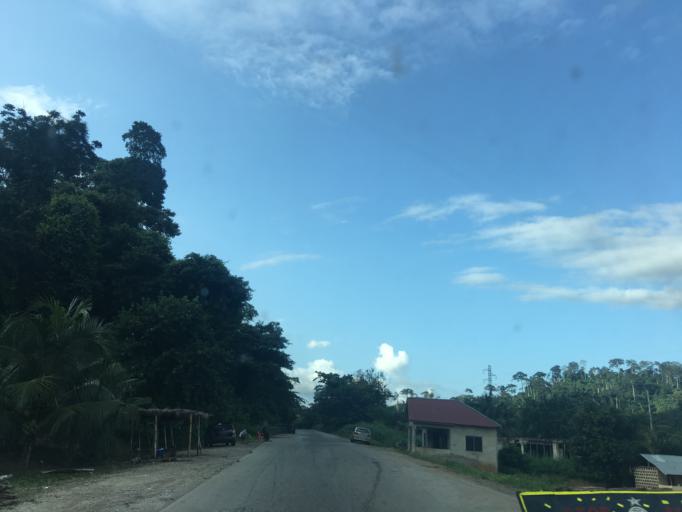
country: GH
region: Western
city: Bibiani
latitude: 6.2760
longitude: -2.2266
